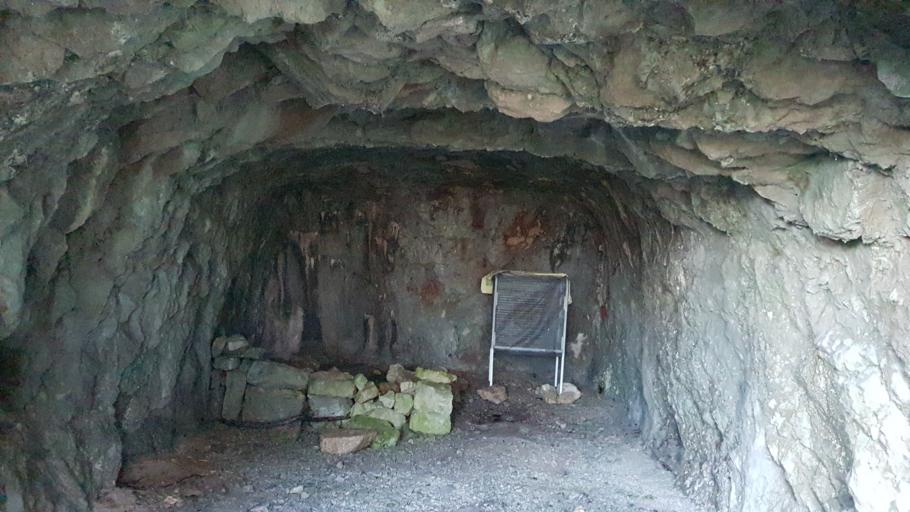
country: IT
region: Trentino-Alto Adige
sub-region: Provincia di Trento
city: Padergnone
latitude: 46.0666
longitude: 10.9592
